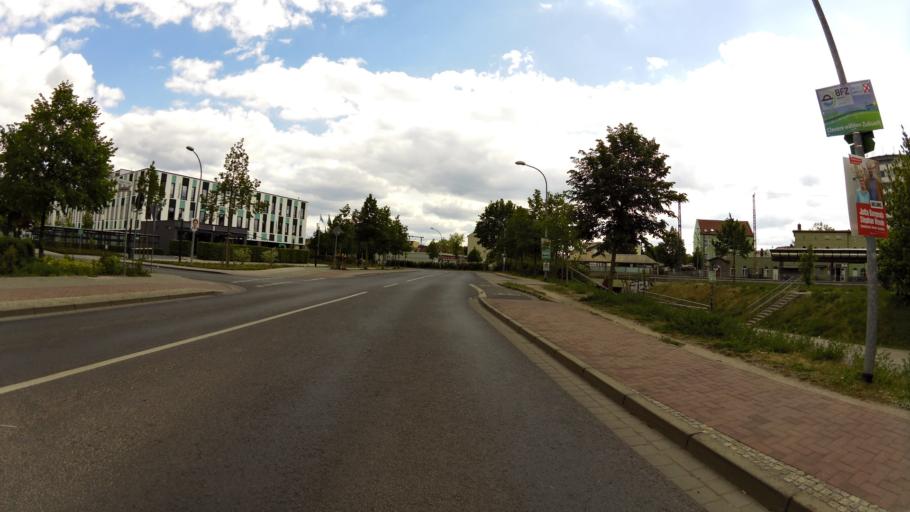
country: DE
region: Brandenburg
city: Furstenwalde
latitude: 52.3674
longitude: 14.0605
